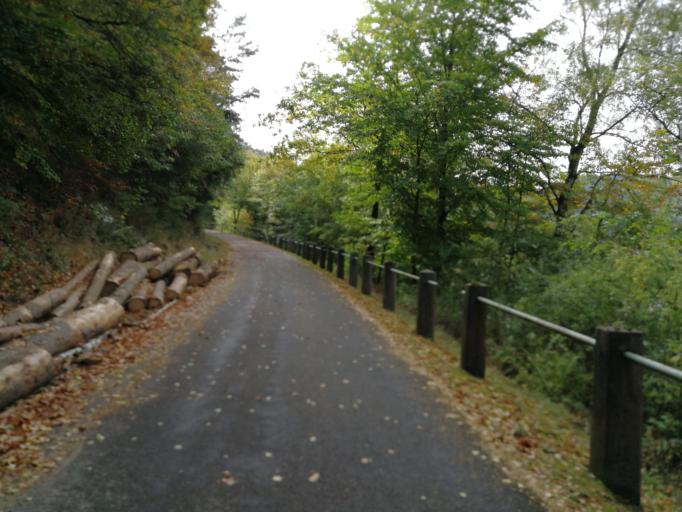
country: DE
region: North Rhine-Westphalia
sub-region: Regierungsbezirk Arnsberg
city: Meschede
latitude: 51.3294
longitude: 8.2665
